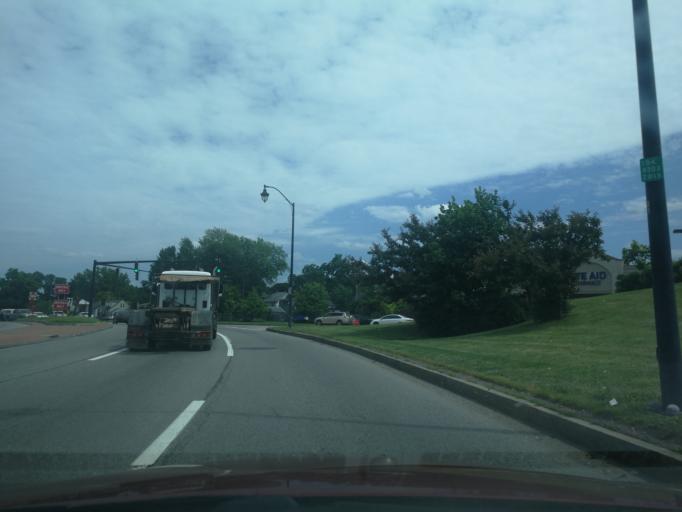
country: US
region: New York
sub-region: Monroe County
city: Rochester
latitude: 43.1944
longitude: -77.6285
